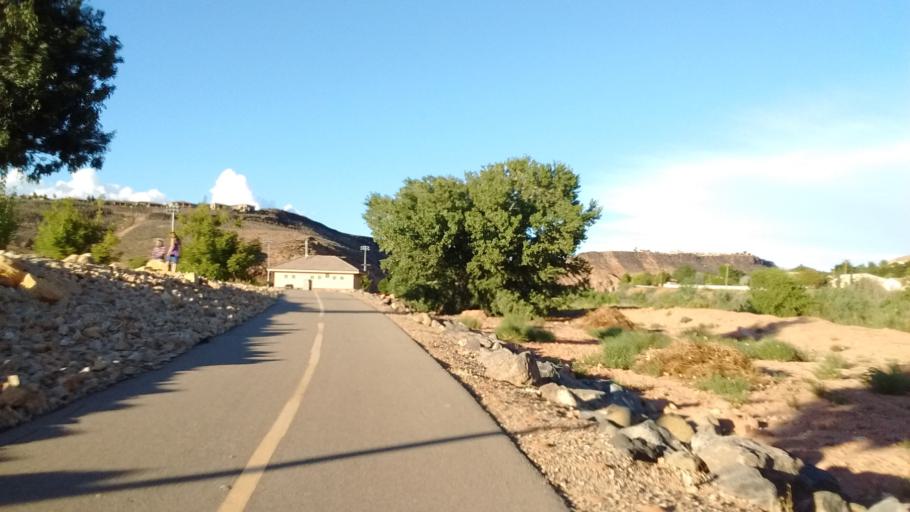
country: US
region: Utah
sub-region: Washington County
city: Washington
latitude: 37.1173
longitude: -113.5013
